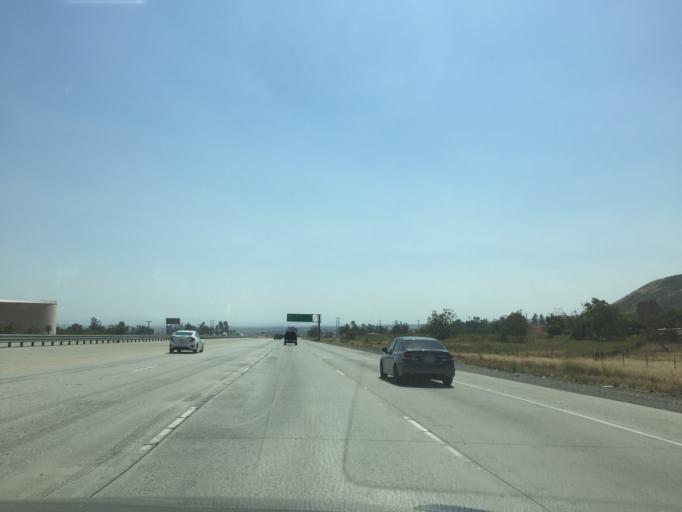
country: US
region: California
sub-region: San Bernardino County
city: Fontana
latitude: 34.1742
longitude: -117.4486
